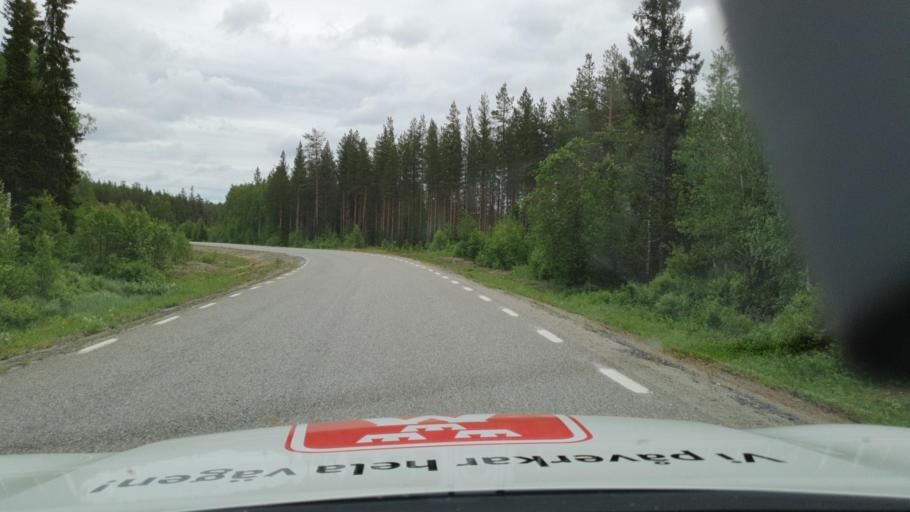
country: SE
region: Vaesterbotten
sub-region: Lycksele Kommun
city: Lycksele
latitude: 64.1951
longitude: 18.3025
